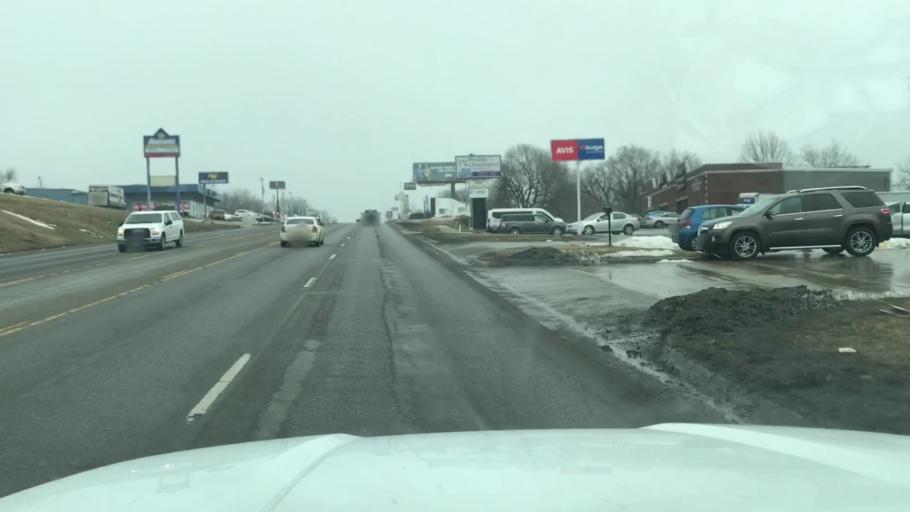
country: US
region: Missouri
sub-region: Buchanan County
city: Saint Joseph
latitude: 39.7486
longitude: -94.8024
